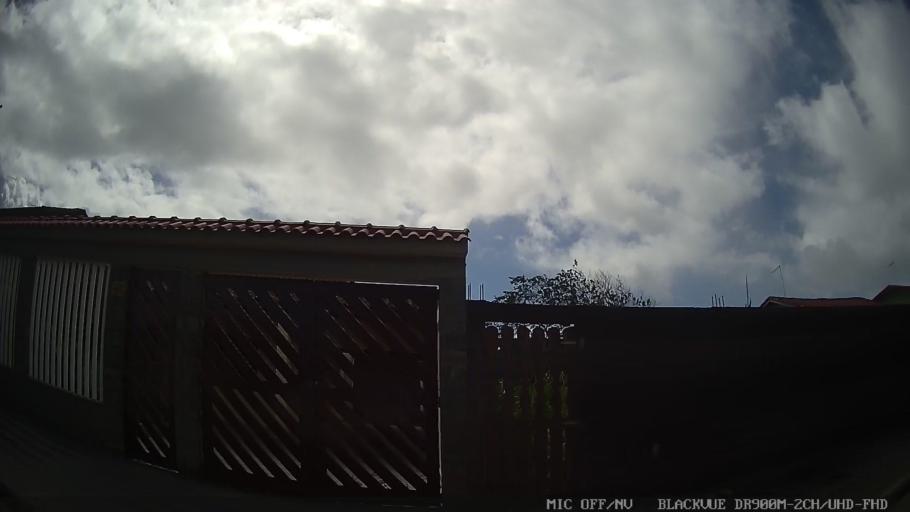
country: BR
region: Sao Paulo
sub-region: Itanhaem
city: Itanhaem
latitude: -24.2265
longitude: -46.8647
